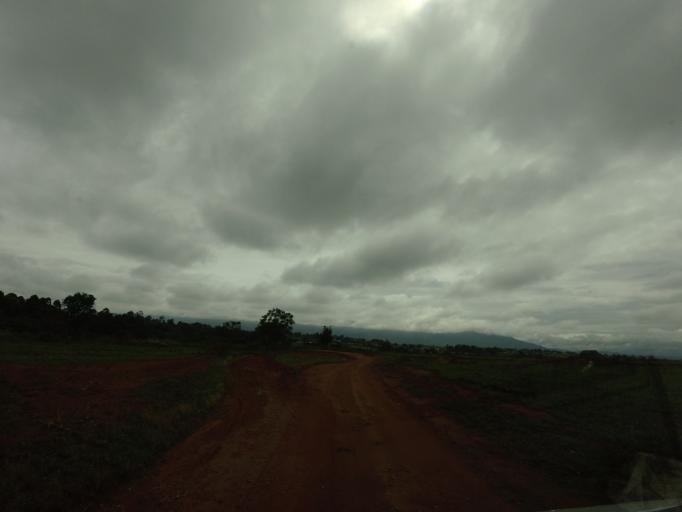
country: SZ
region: Hhohho
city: Lobamba
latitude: -26.4615
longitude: 31.1869
